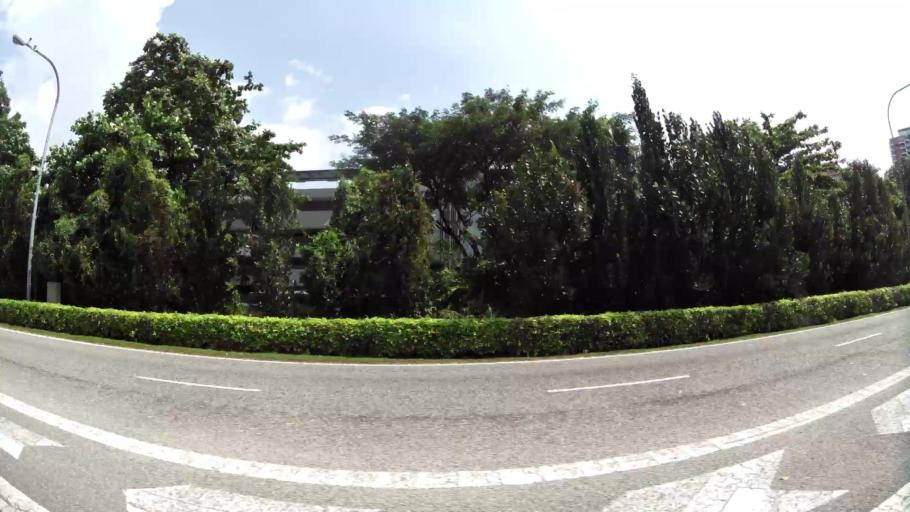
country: SG
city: Singapore
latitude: 1.2803
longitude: 103.8301
